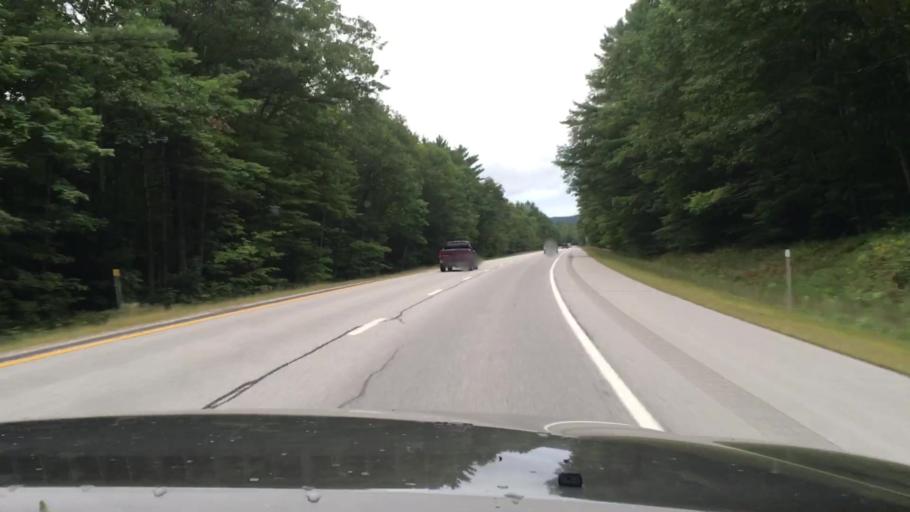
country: US
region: New Hampshire
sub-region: Belknap County
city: Sanbornton
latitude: 43.5330
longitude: -71.6147
